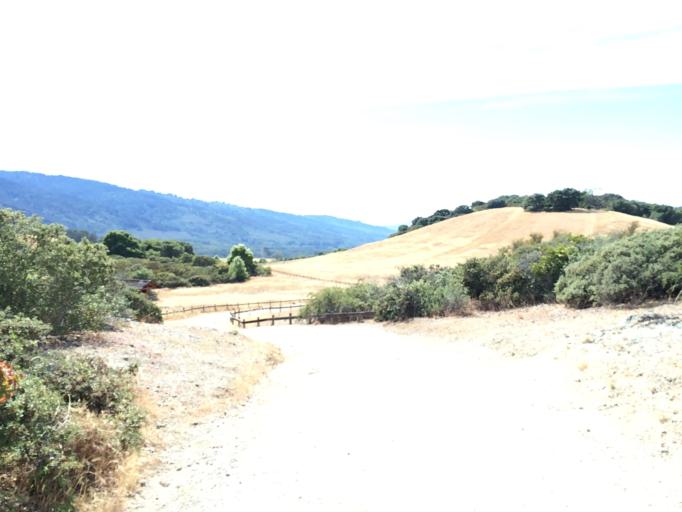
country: US
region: California
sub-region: San Mateo County
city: Emerald Lake Hills
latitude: 37.4622
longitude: -122.2779
